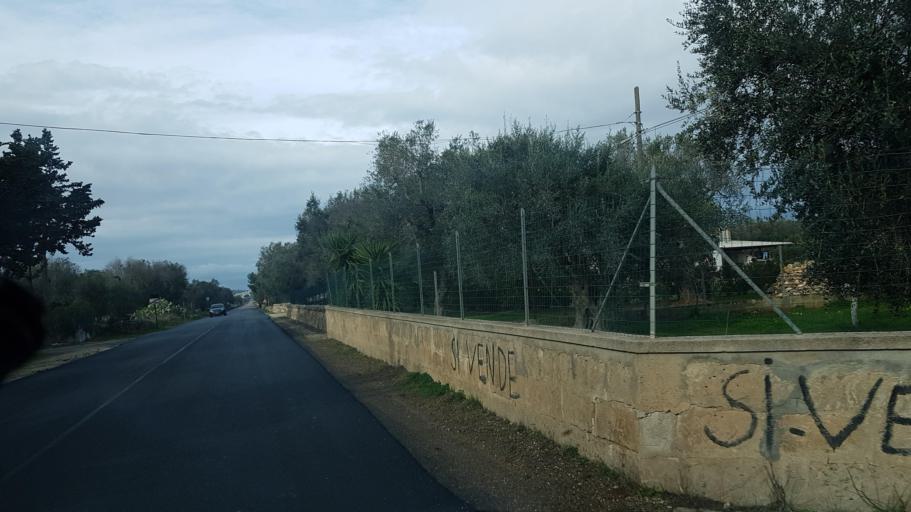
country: IT
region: Apulia
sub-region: Provincia di Brindisi
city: Oria
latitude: 40.4844
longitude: 17.6779
